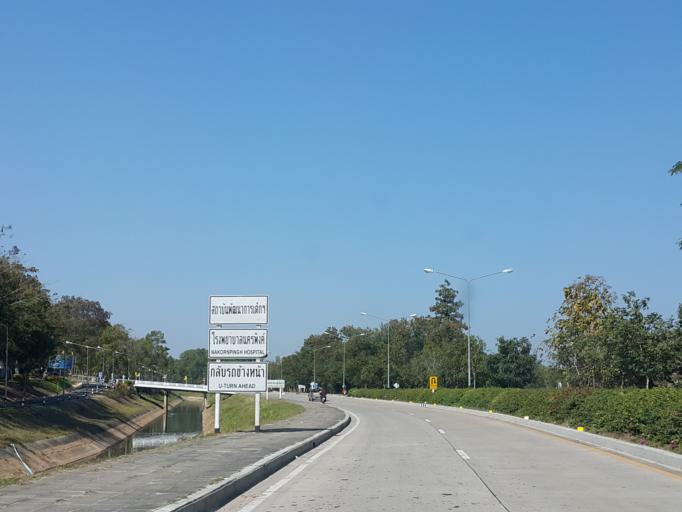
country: TH
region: Chiang Mai
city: Chiang Mai
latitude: 18.8522
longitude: 98.9617
